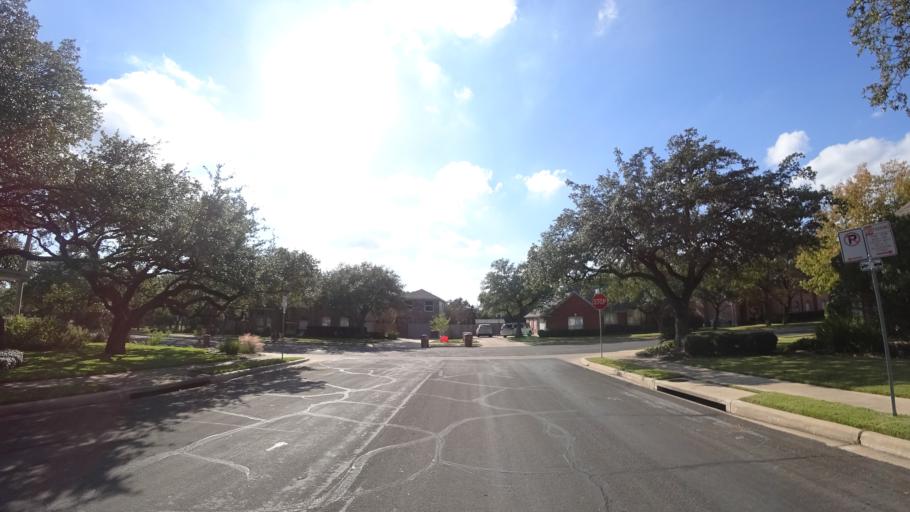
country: US
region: Texas
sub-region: Travis County
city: Shady Hollow
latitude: 30.1805
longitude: -97.8594
